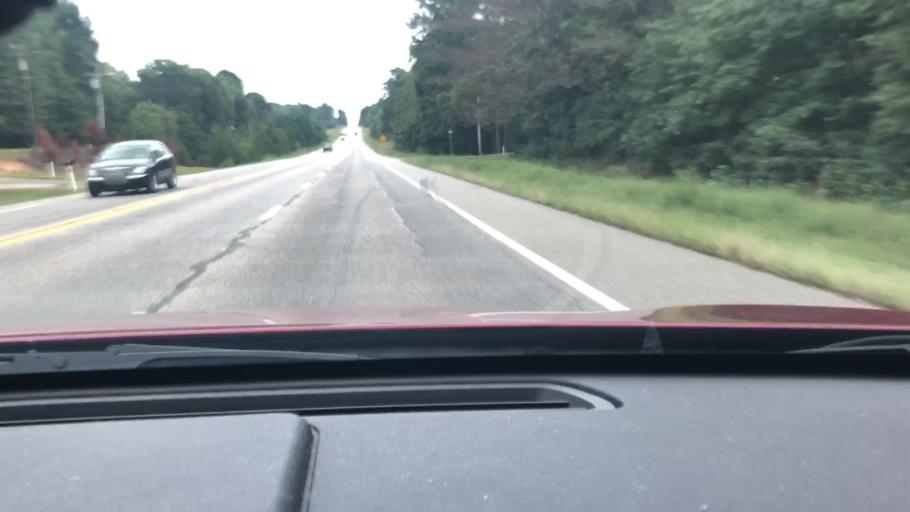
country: US
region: Arkansas
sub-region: Miller County
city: Texarkana
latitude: 33.4295
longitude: -93.9495
